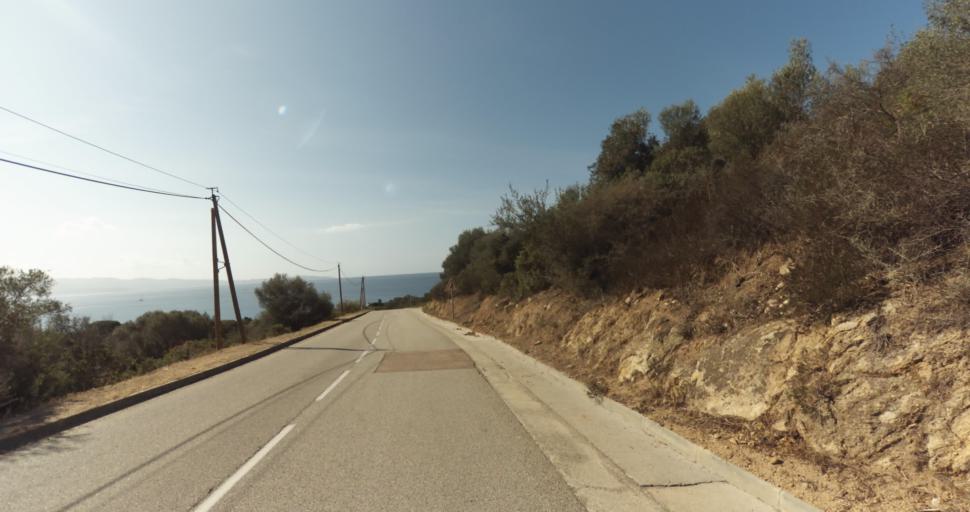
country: FR
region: Corsica
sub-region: Departement de la Corse-du-Sud
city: Ajaccio
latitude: 41.9138
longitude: 8.6437
